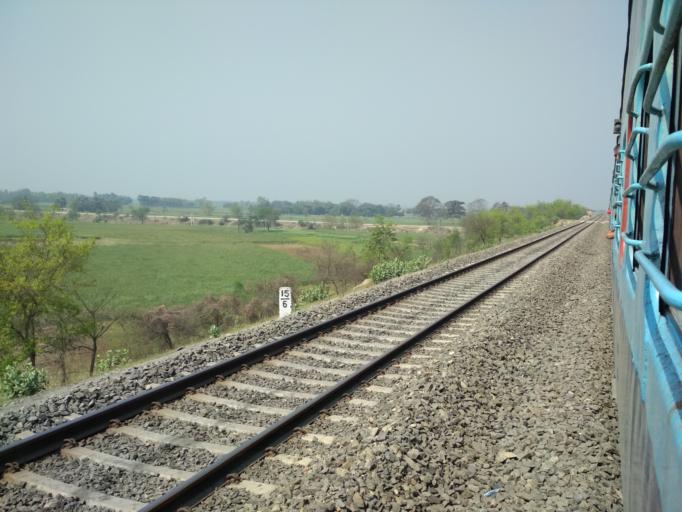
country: IN
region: Bihar
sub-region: Munger
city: Munger
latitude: 25.4360
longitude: 86.4359
